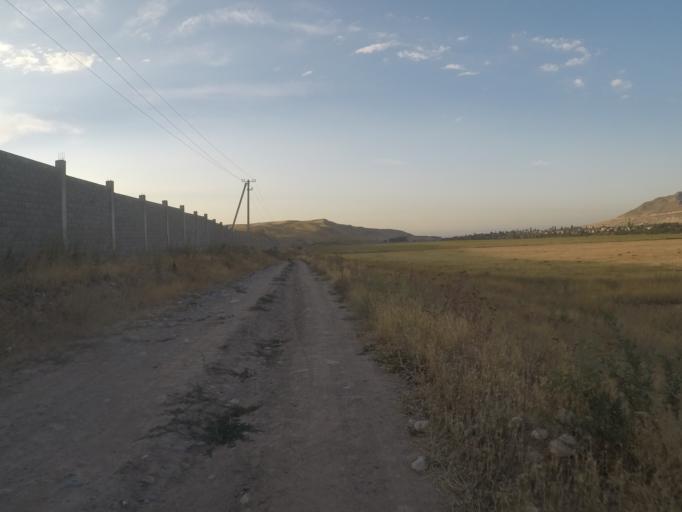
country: KG
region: Chuy
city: Bishkek
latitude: 42.7522
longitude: 74.6369
